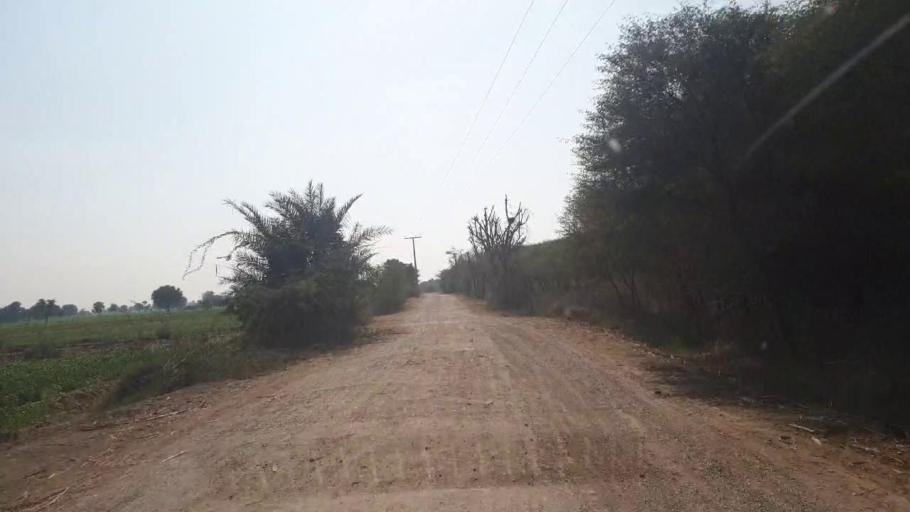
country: PK
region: Sindh
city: Shahdadpur
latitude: 26.0447
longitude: 68.4628
